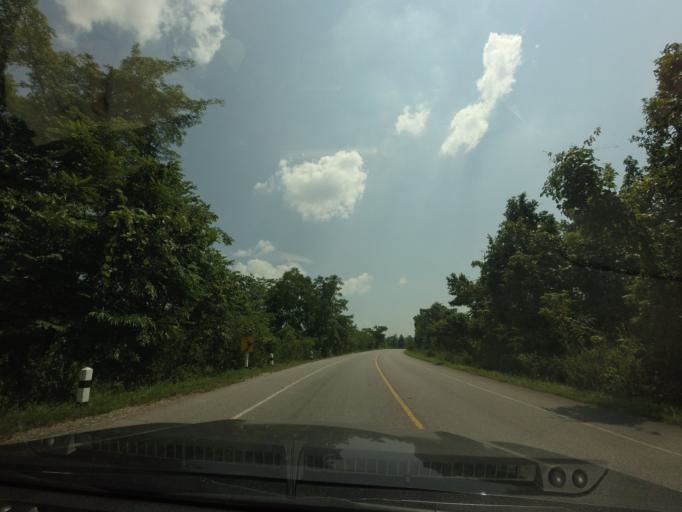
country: TH
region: Uttaradit
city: Thong Saen Khan
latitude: 17.3214
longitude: 100.3881
